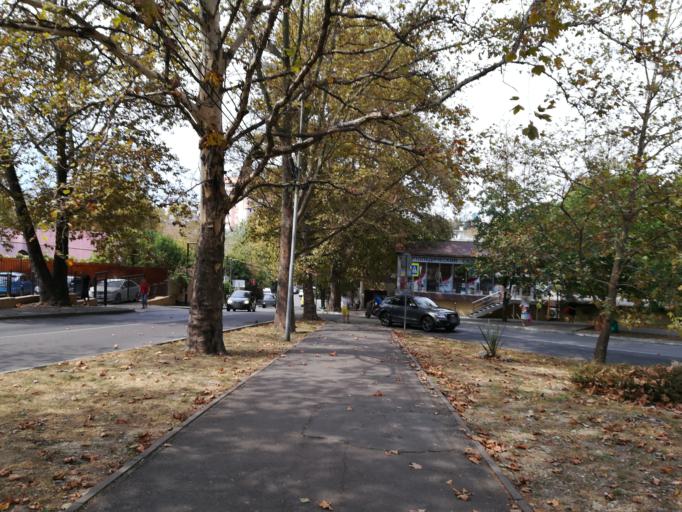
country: RU
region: Krasnodarskiy
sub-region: Sochi City
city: Sochi
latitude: 43.5943
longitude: 39.7360
